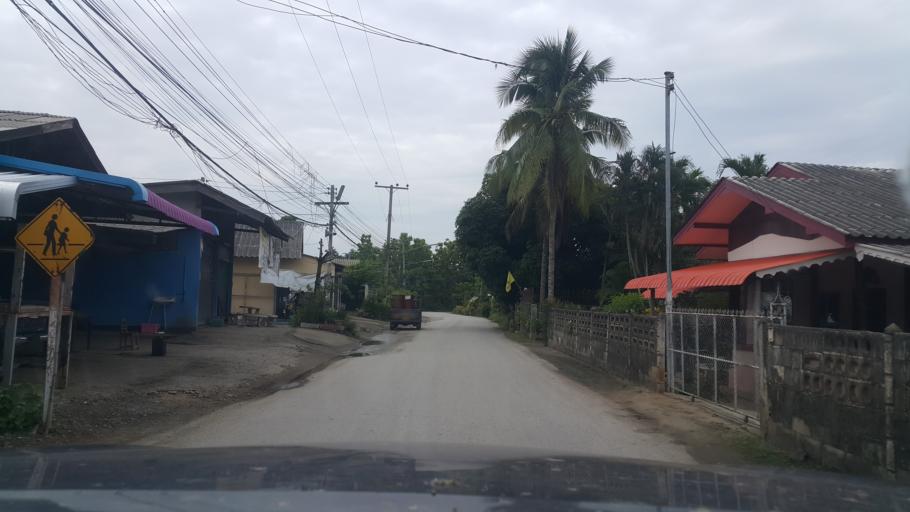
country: TH
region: Chiang Mai
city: San Pa Tong
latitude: 18.6665
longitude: 98.8349
